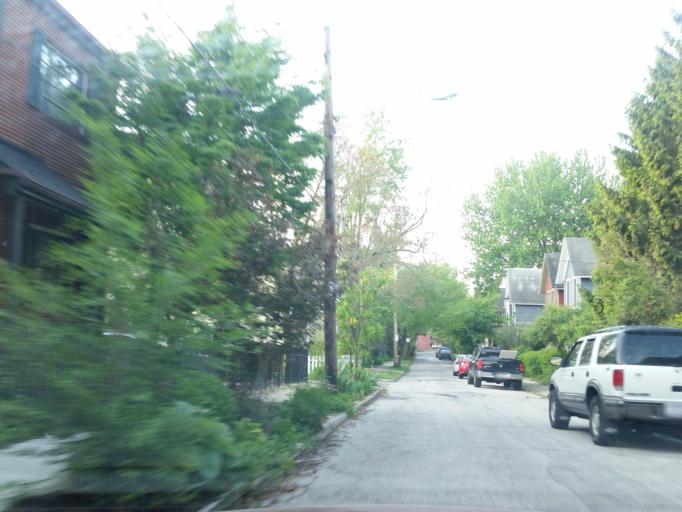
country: US
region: Ohio
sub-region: Cuyahoga County
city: Cleveland
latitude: 41.4862
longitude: -81.7109
